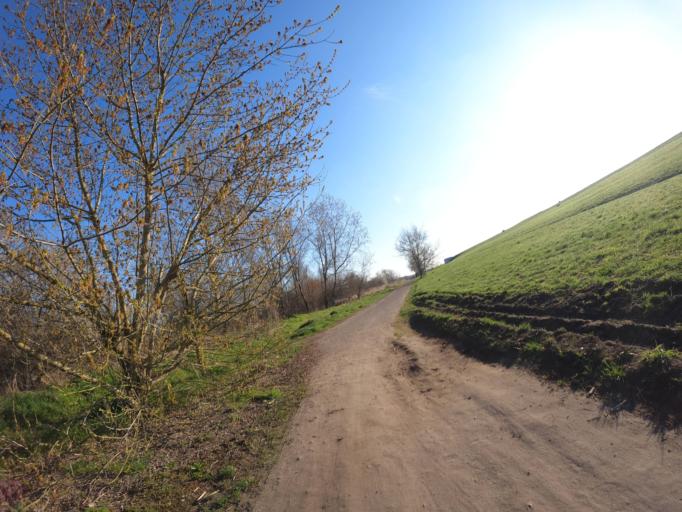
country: DE
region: Berlin
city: Gropiusstadt
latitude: 52.4112
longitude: 13.4504
